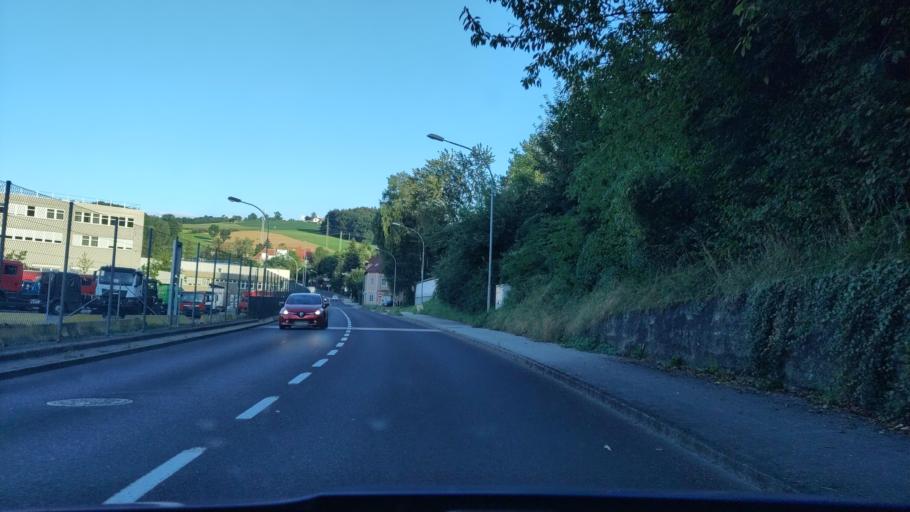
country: AT
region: Upper Austria
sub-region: Steyr Stadt
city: Steyr
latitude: 48.0367
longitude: 14.4273
